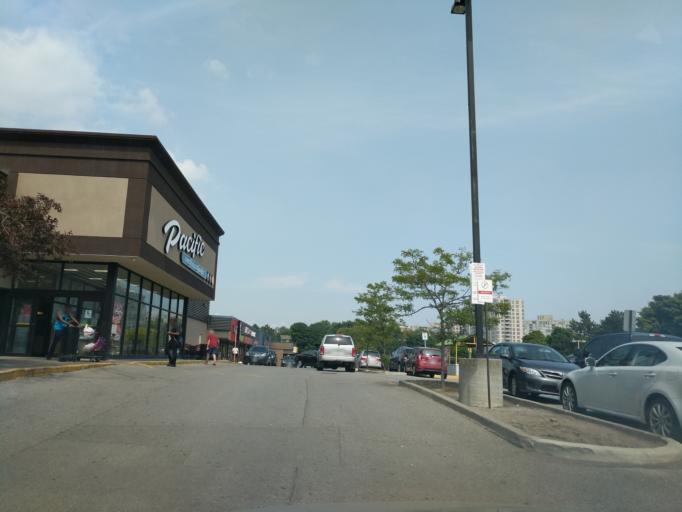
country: CA
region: Ontario
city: Ajax
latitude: 43.8375
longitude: -79.0895
